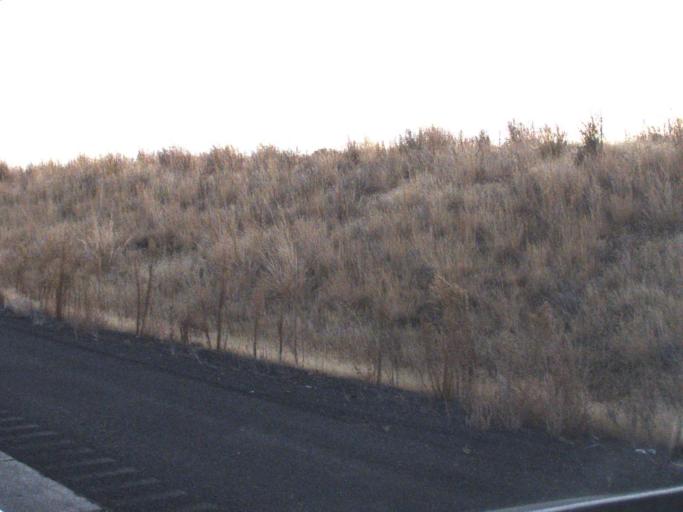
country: US
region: Washington
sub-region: Franklin County
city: Connell
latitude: 46.7968
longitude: -118.7394
